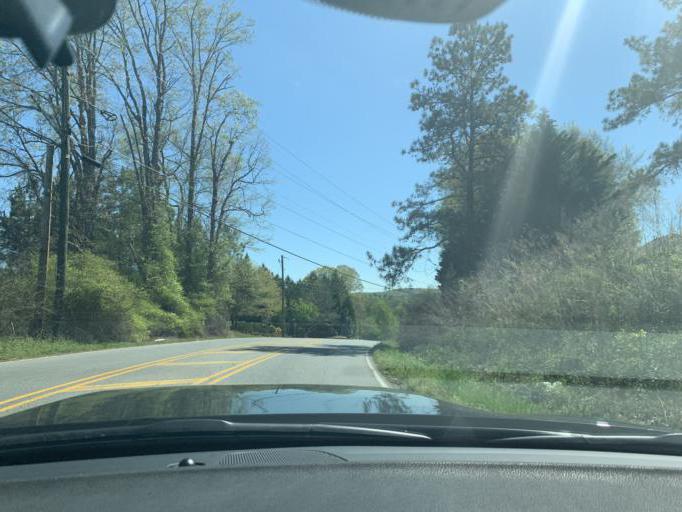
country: US
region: Georgia
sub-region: Fulton County
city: Milton
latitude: 34.1351
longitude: -84.2228
